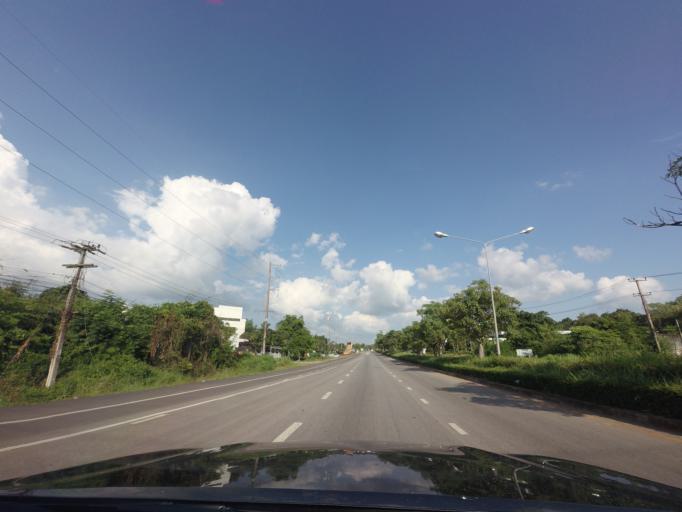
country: TH
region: Nong Khai
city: Nong Khai
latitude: 17.8876
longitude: 102.7652
